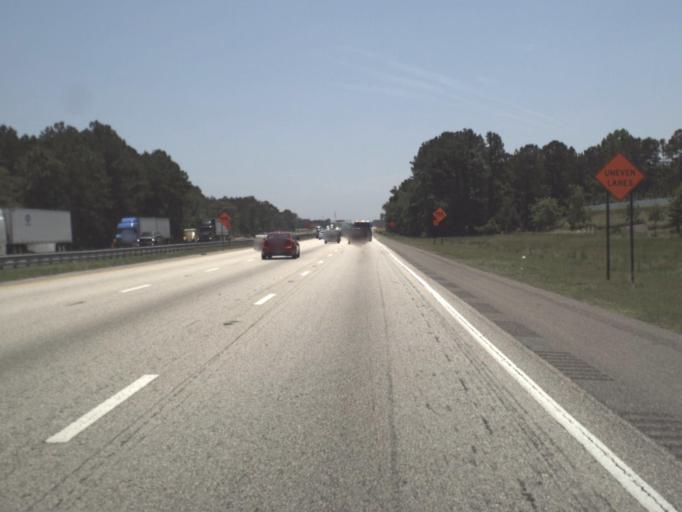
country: US
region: Florida
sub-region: Saint Johns County
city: Fruit Cove
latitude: 30.1292
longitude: -81.5288
